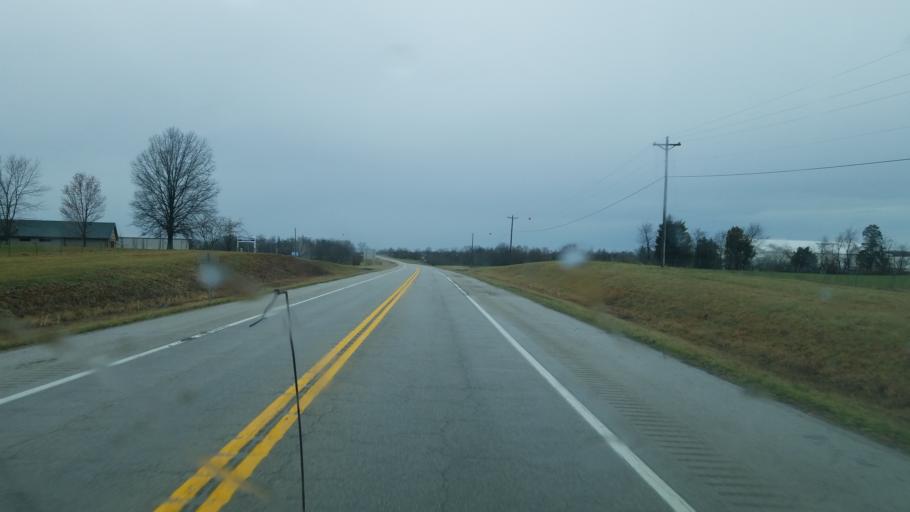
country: US
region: Ohio
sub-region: Adams County
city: Manchester
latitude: 38.5564
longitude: -83.5911
